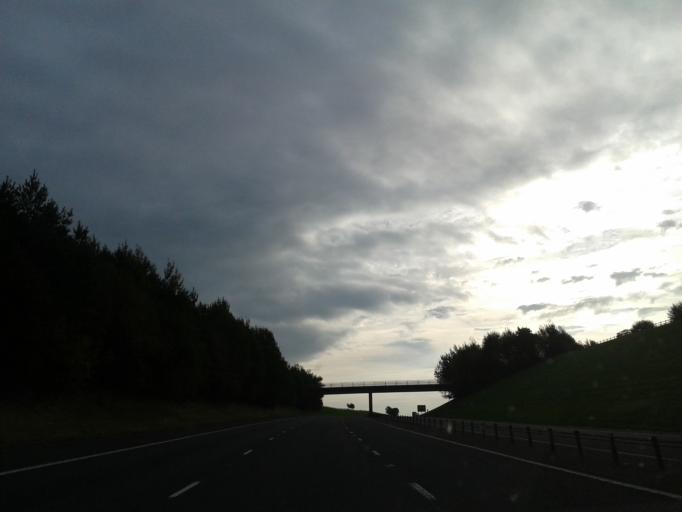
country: GB
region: Scotland
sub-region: Dumfries and Galloway
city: Annan
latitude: 55.0557
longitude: -3.2400
